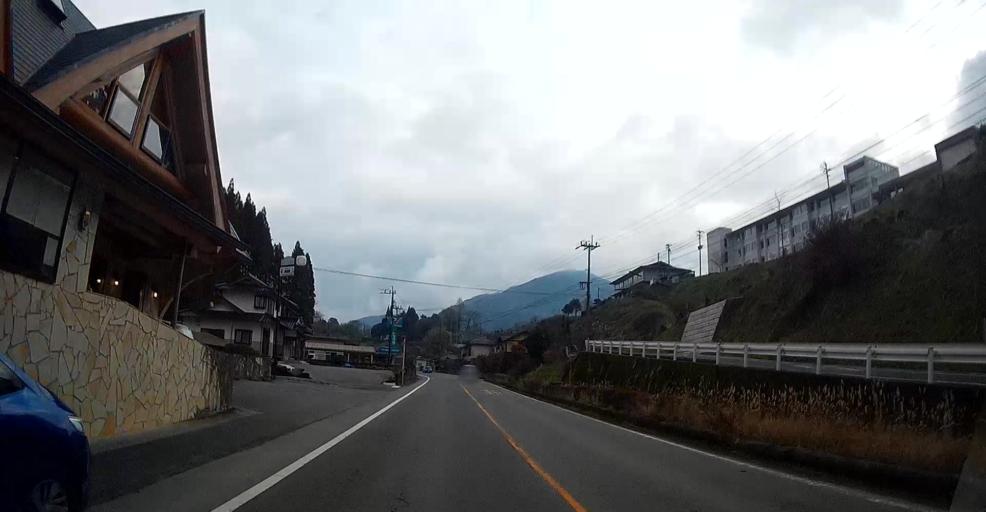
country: JP
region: Kumamoto
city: Matsubase
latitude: 32.6211
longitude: 130.8671
